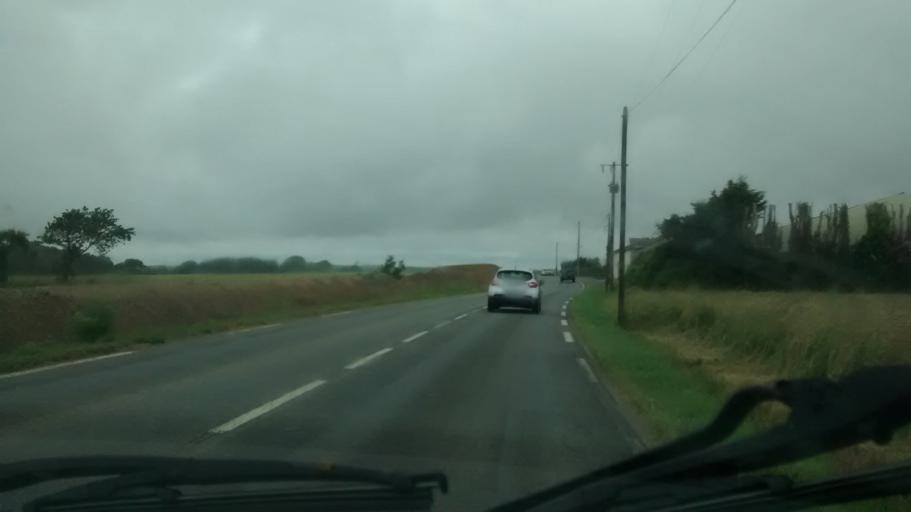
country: FR
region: Brittany
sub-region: Departement du Morbihan
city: Ploemeur
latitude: 47.7538
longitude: -3.4202
